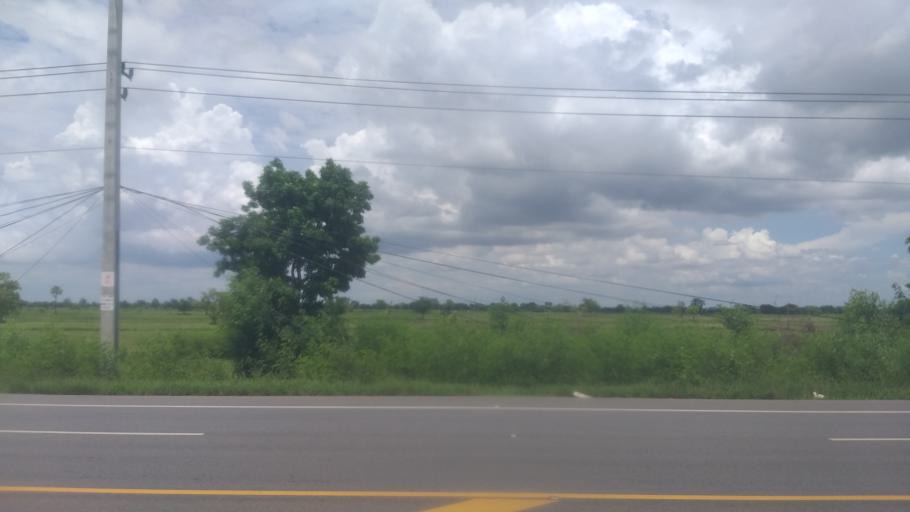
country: TH
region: Nakhon Ratchasima
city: Non Thai
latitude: 15.1213
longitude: 102.1026
